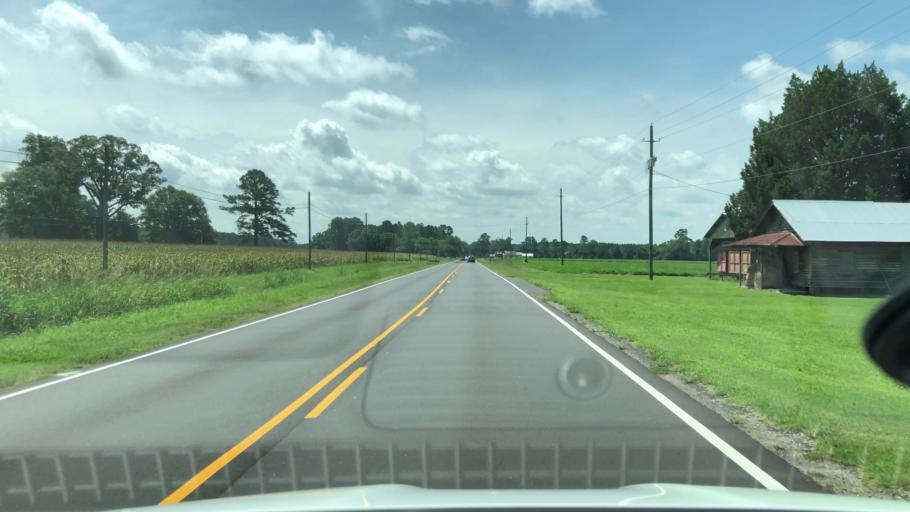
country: US
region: North Carolina
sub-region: Martin County
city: Williamston
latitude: 35.7491
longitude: -77.0760
